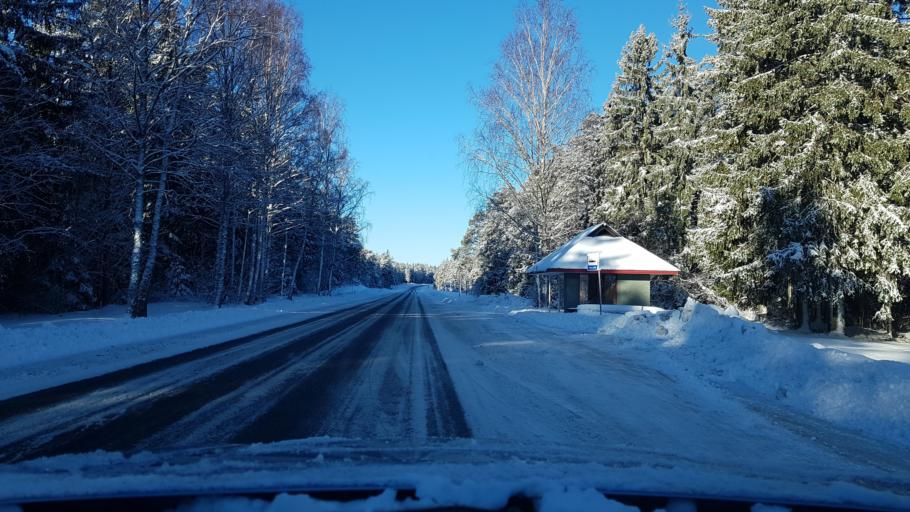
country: EE
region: Hiiumaa
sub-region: Kaerdla linn
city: Kardla
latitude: 58.9626
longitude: 22.8441
